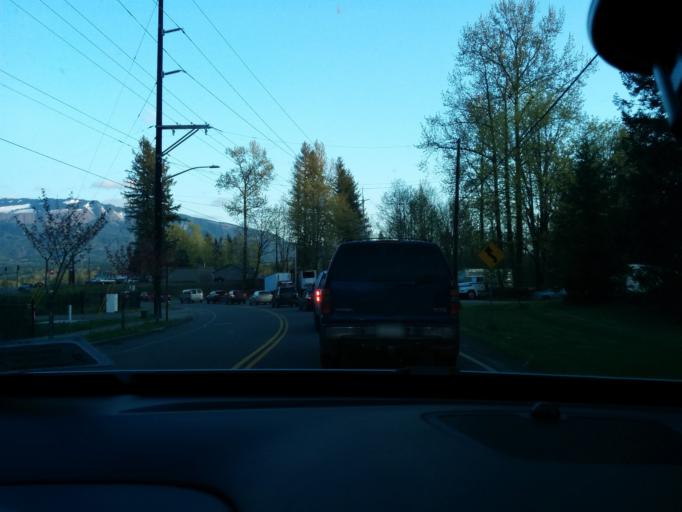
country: US
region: Washington
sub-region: Snohomish County
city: Sultan
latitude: 47.8669
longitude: -121.7992
